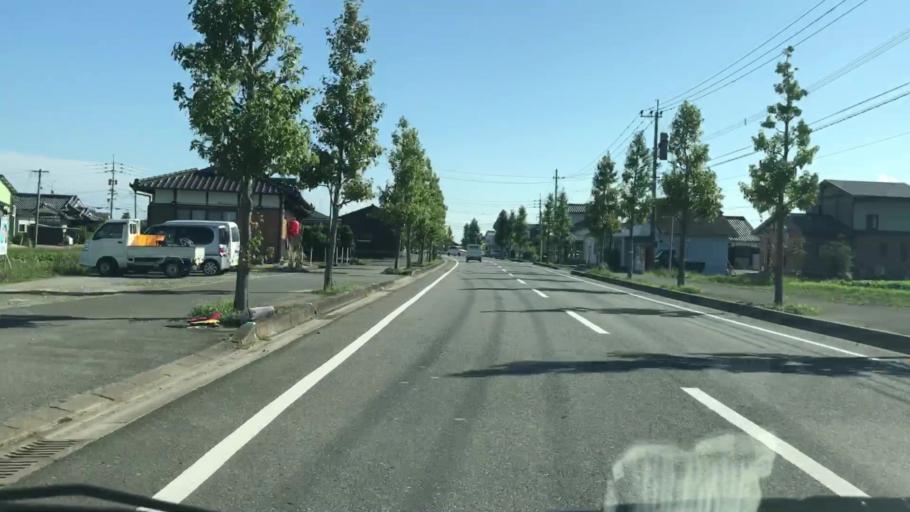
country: JP
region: Saga Prefecture
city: Okawa
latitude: 33.1898
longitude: 130.3147
